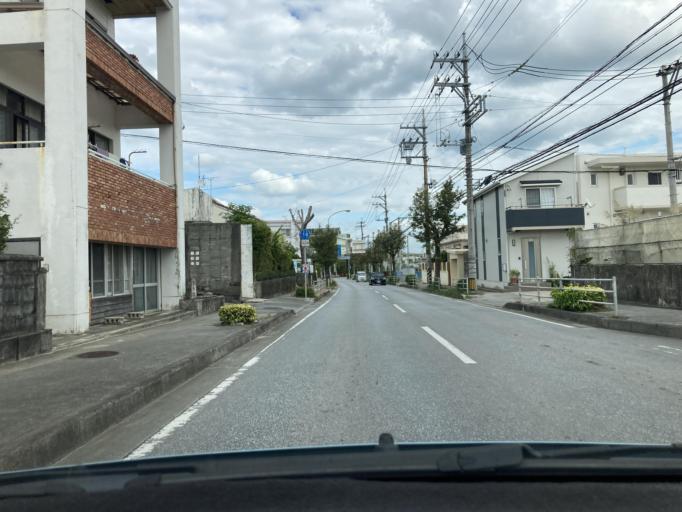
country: JP
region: Okinawa
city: Gushikawa
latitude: 26.3493
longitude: 127.8468
